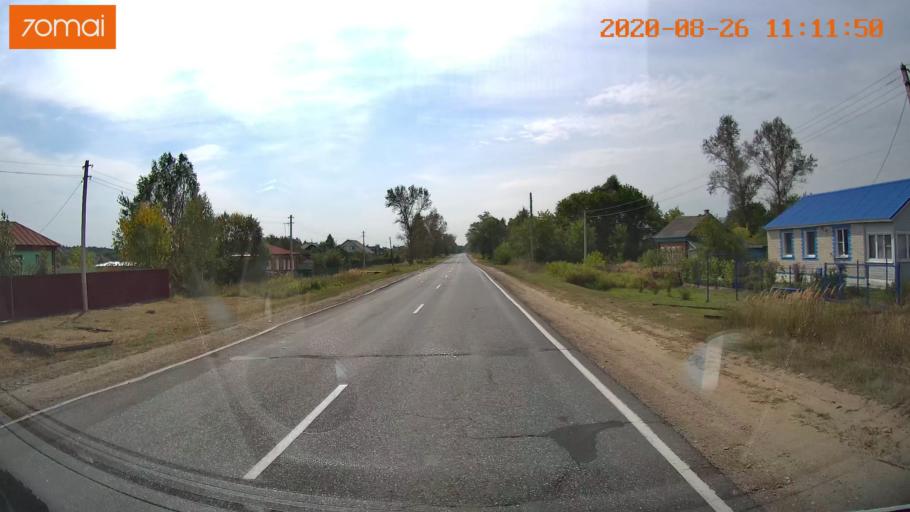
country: RU
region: Rjazan
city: Izhevskoye
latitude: 54.4762
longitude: 41.1259
